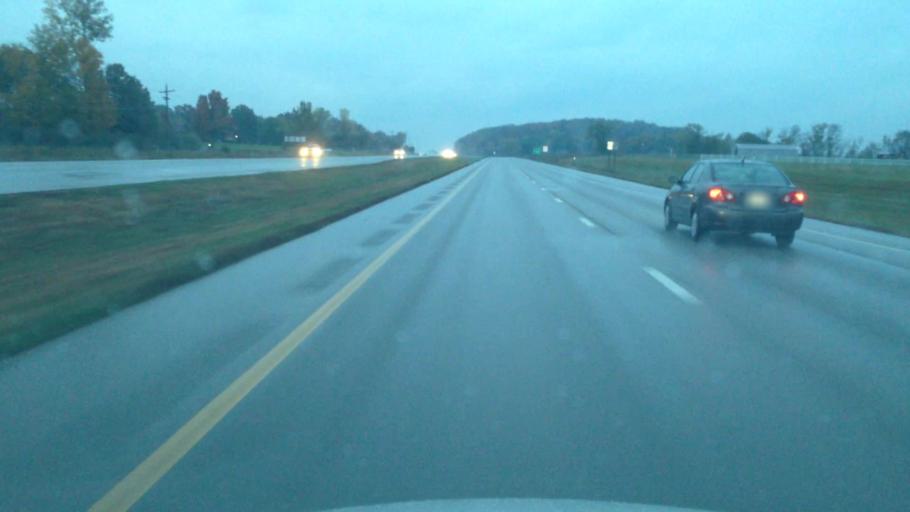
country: US
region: Kansas
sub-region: Douglas County
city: Lawrence
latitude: 38.8985
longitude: -95.2606
